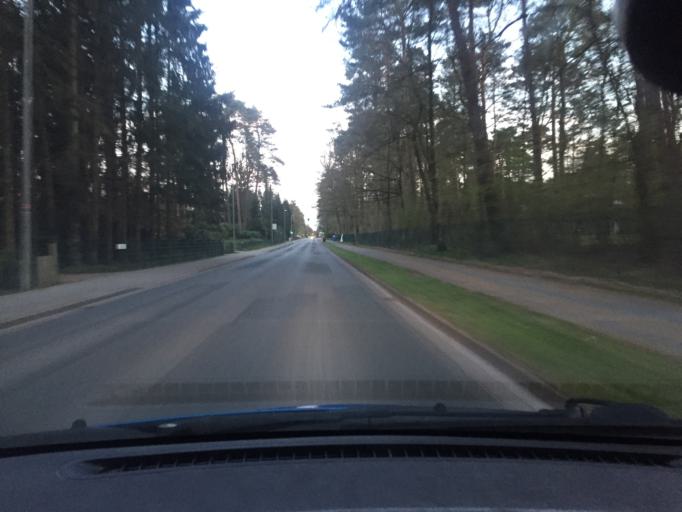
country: DE
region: Lower Saxony
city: Buchholz in der Nordheide
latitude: 53.2932
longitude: 9.8701
